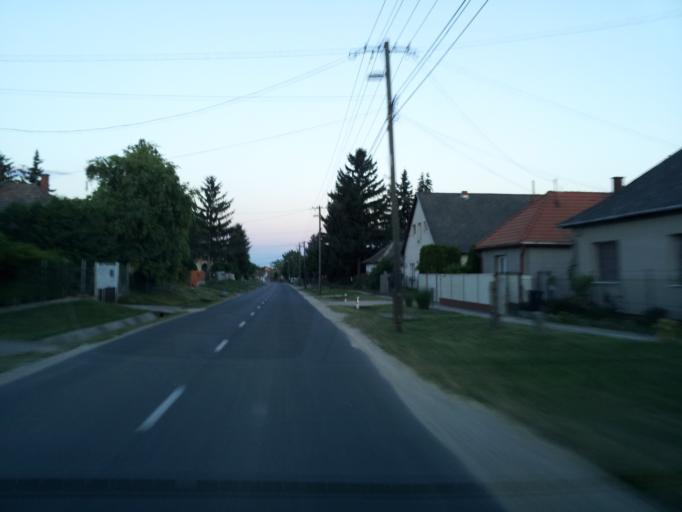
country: HU
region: Veszprem
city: Balatonkenese
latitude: 47.0431
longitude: 18.0980
